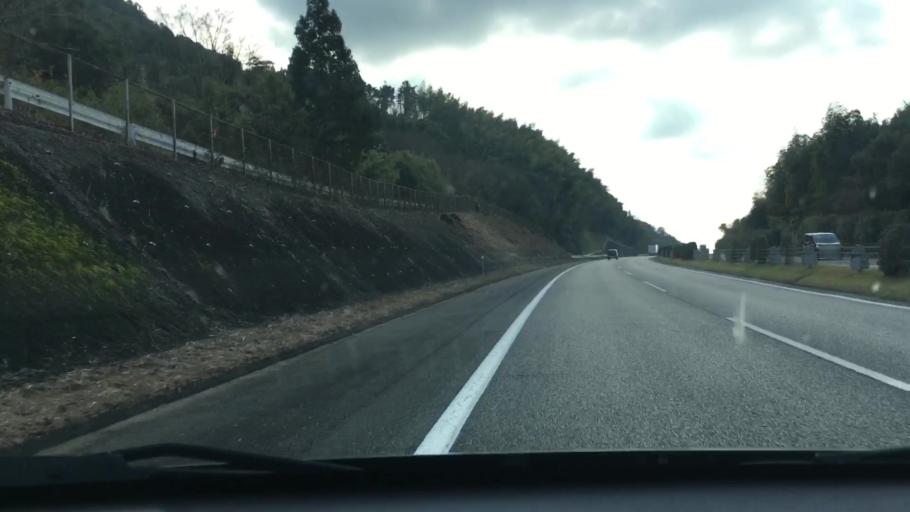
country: JP
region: Kumamoto
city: Yatsushiro
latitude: 32.5327
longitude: 130.6704
